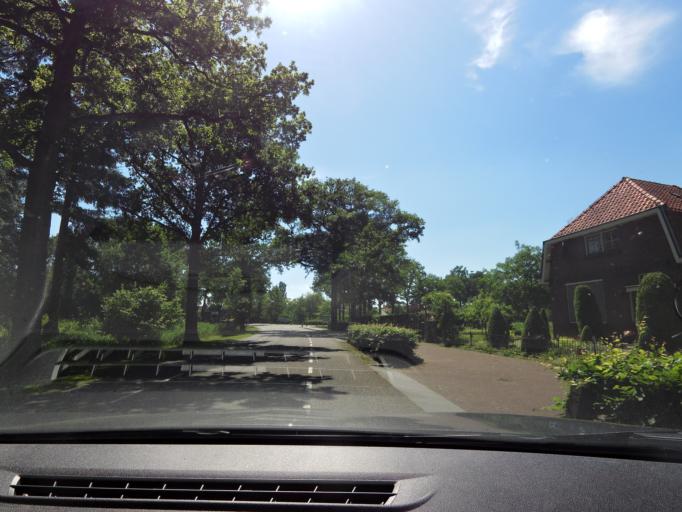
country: NL
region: Overijssel
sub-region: Gemeente Hof van Twente
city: Diepenheim
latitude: 52.2038
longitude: 6.5617
